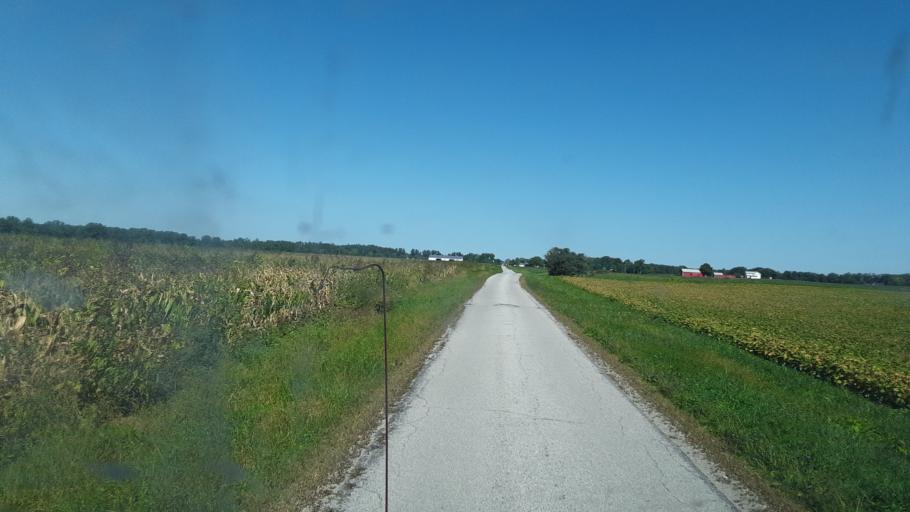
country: US
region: Ohio
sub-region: Sandusky County
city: Mount Carmel
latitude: 41.1672
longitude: -82.8997
